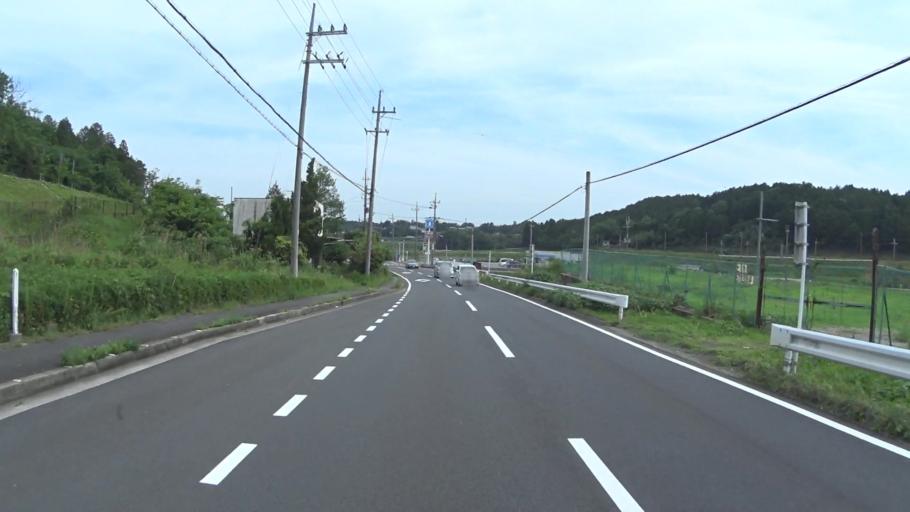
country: JP
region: Shiga Prefecture
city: Kitahama
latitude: 35.1378
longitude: 135.8821
